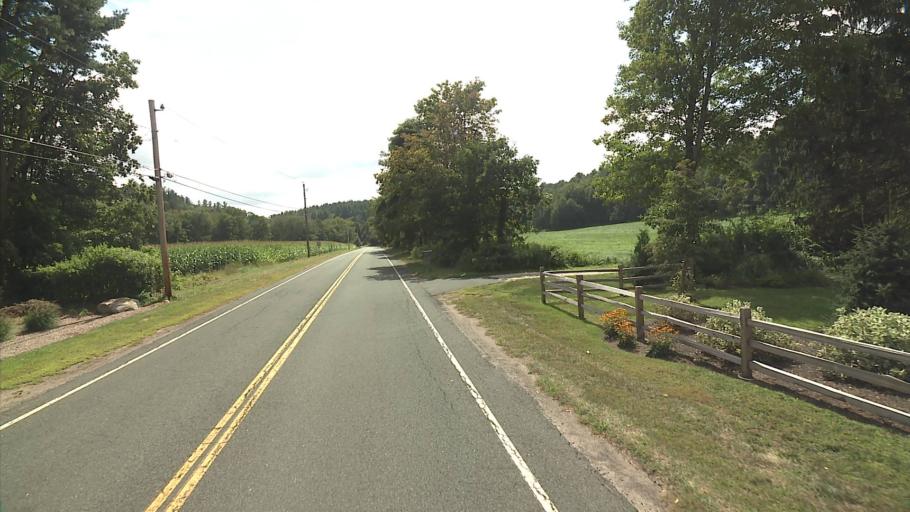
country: US
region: Connecticut
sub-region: Hartford County
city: North Granby
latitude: 42.0225
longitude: -72.8596
